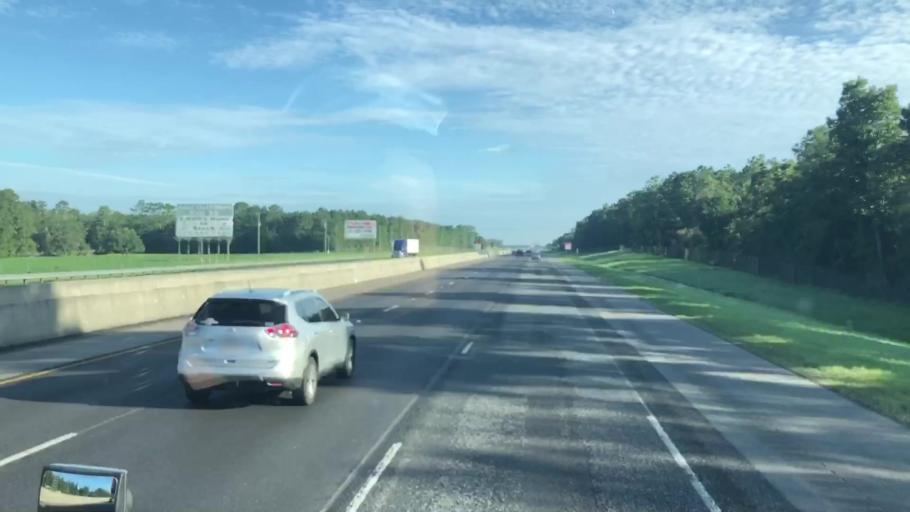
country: US
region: Georgia
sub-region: Lowndes County
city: Hahira
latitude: 30.9393
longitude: -83.3717
